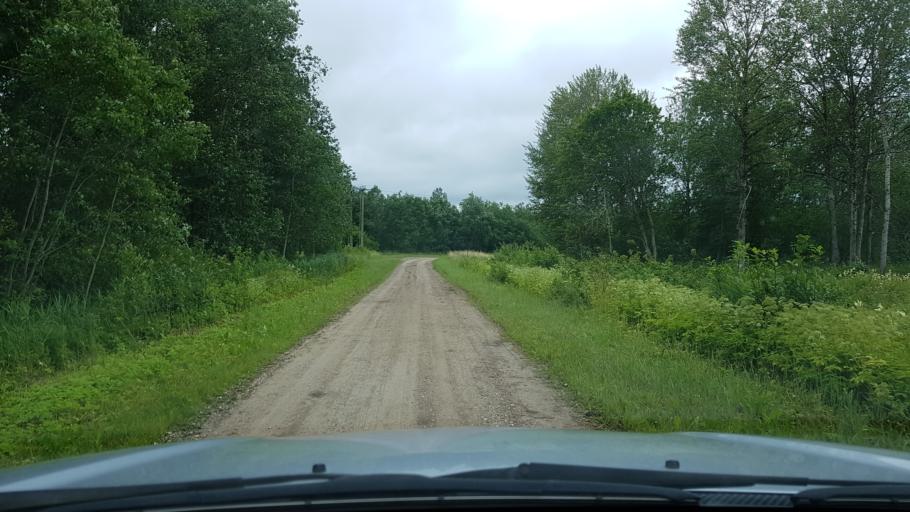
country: EE
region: Ida-Virumaa
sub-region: Narva-Joesuu linn
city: Narva-Joesuu
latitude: 59.3644
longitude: 27.9224
